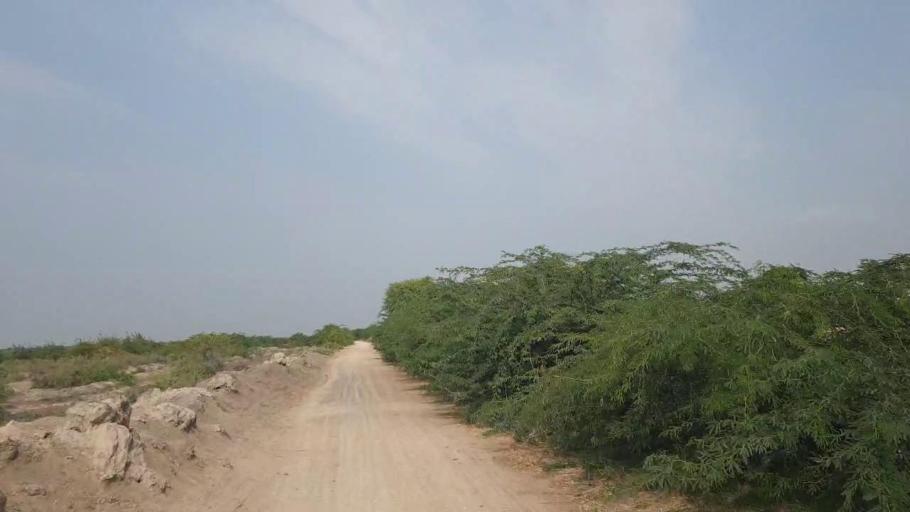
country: PK
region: Sindh
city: Badin
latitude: 24.5628
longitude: 68.7335
